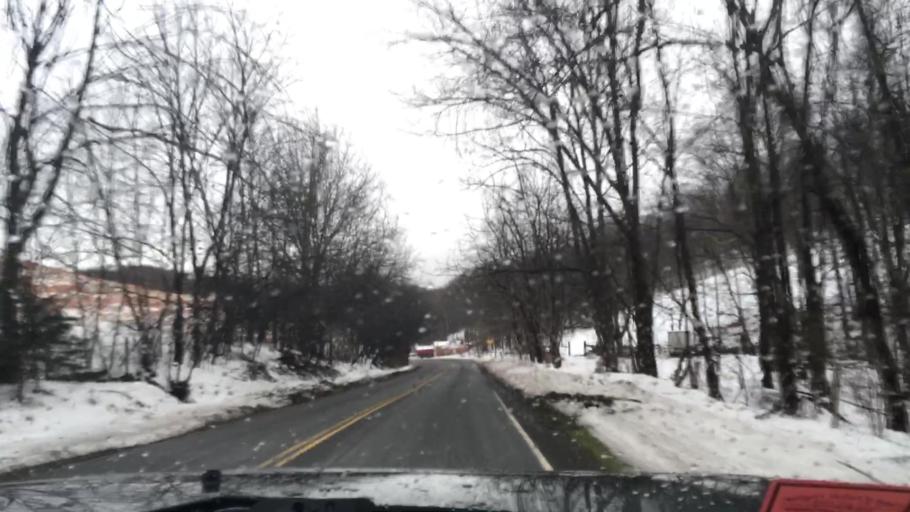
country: US
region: Virginia
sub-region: Pulaski County
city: Pulaski
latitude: 37.0117
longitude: -80.6932
